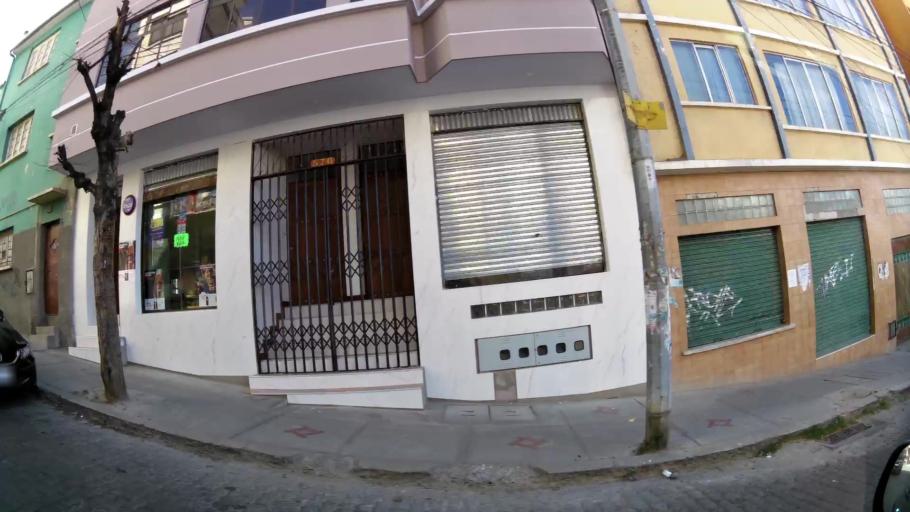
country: BO
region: La Paz
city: La Paz
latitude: -16.5064
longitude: -68.1340
